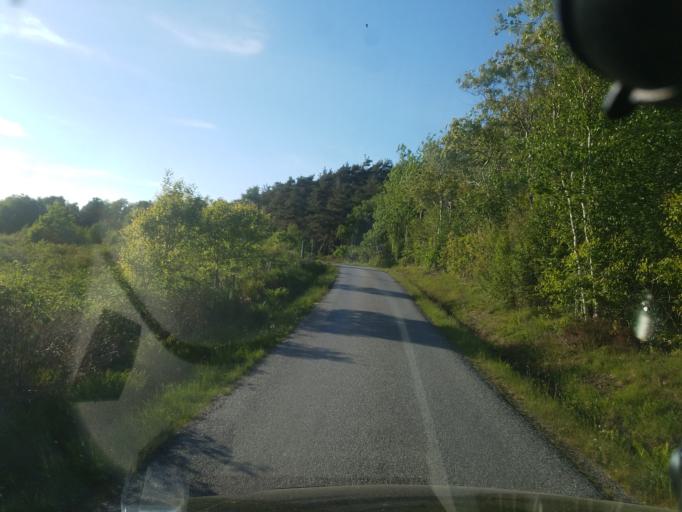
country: SE
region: Vaestra Goetaland
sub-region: Lysekils Kommun
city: Lysekil
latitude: 58.3009
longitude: 11.4674
